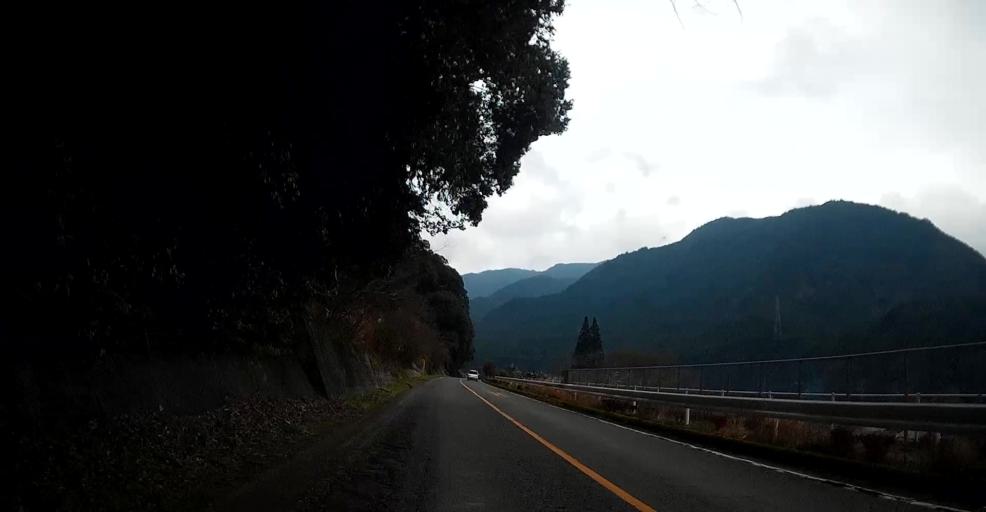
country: JP
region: Kumamoto
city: Matsubase
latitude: 32.6155
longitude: 130.8426
